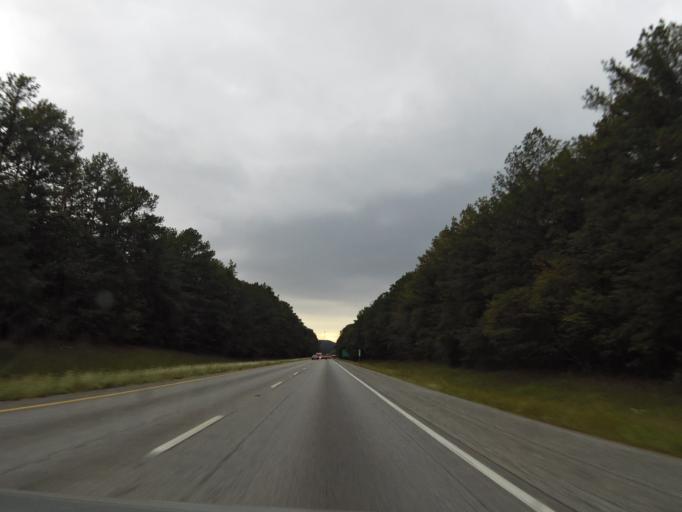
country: US
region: Alabama
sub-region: Saint Clair County
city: Springville
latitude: 33.7815
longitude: -86.4128
